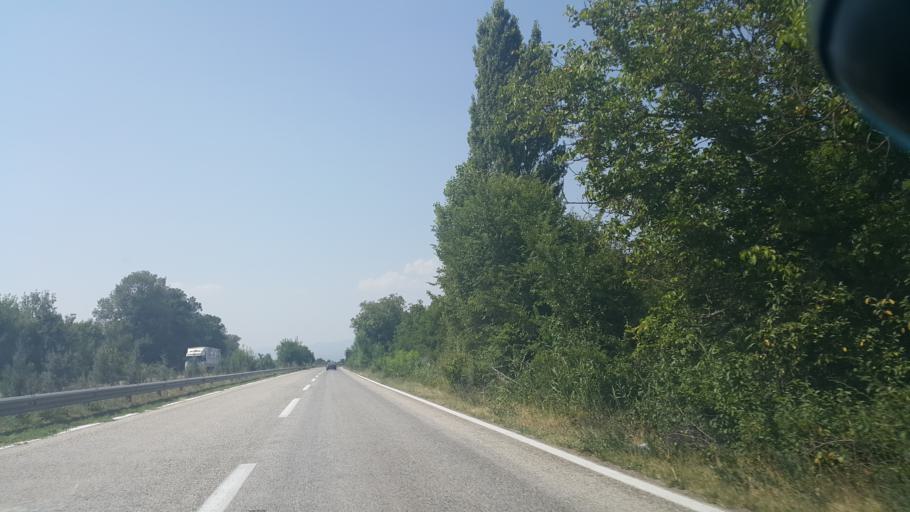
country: MK
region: Petrovec
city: Petrovec
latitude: 41.9181
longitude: 21.6391
